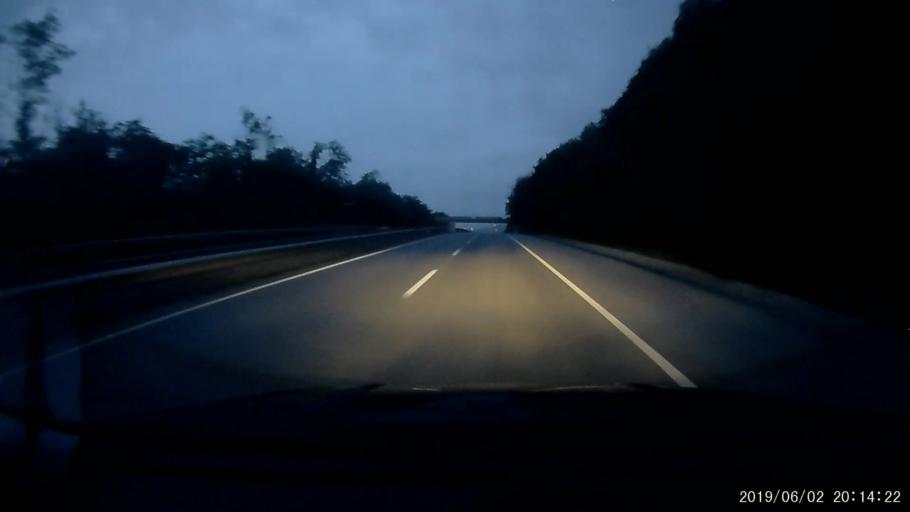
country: TR
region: Giresun
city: Eynesil
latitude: 41.0516
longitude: 39.1189
